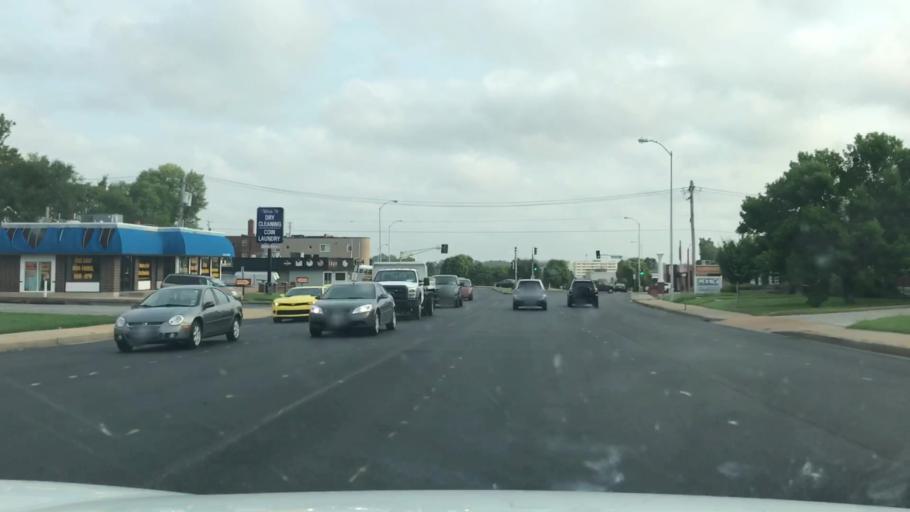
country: US
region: Missouri
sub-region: Saint Louis County
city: Richmond Heights
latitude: 38.6111
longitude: -90.2880
